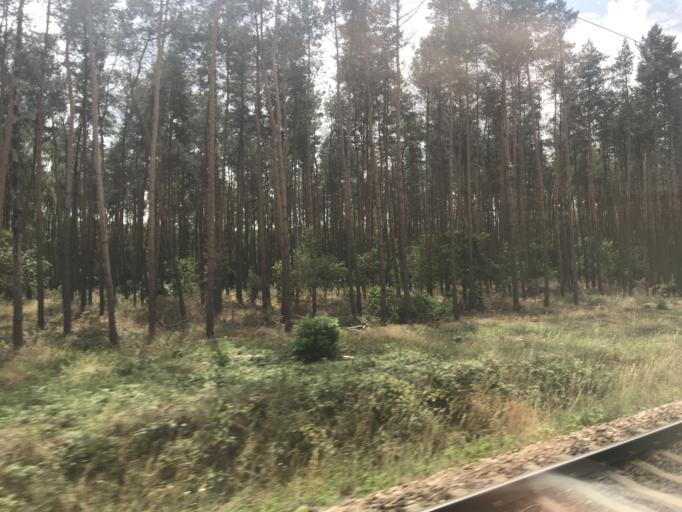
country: PL
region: Greater Poland Voivodeship
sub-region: Powiat poznanski
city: Dopiewo
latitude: 52.3483
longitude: 16.6620
